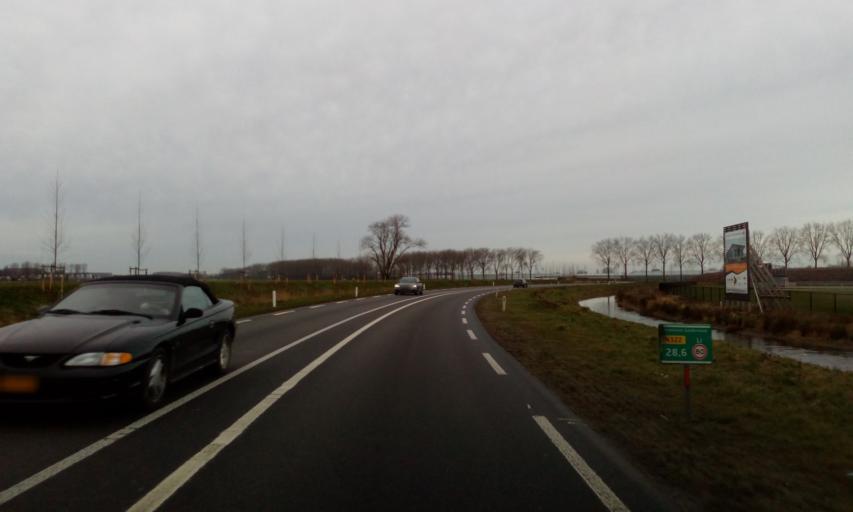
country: NL
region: Gelderland
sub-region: Gemeente Zaltbommel
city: Zaltbommel
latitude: 51.7960
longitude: 5.2381
